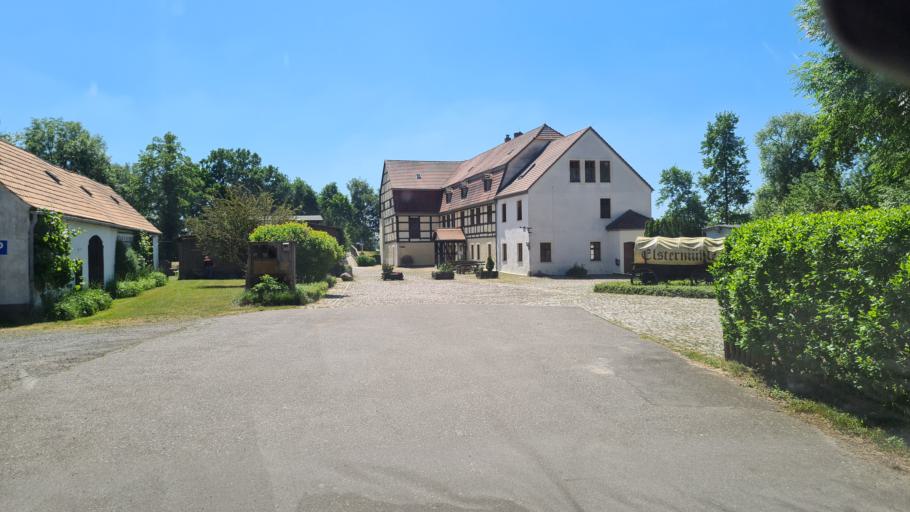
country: DE
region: Brandenburg
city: Plessa
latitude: 51.4634
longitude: 13.6296
